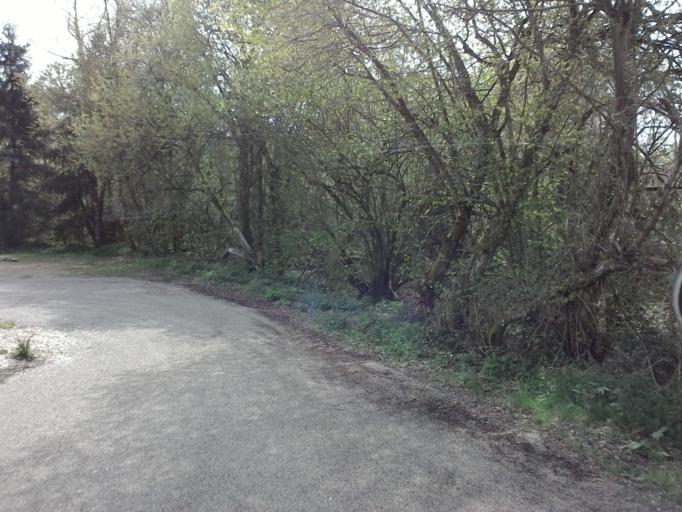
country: FR
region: Bourgogne
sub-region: Departement de la Cote-d'Or
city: Saulieu
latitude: 47.1878
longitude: 4.0736
